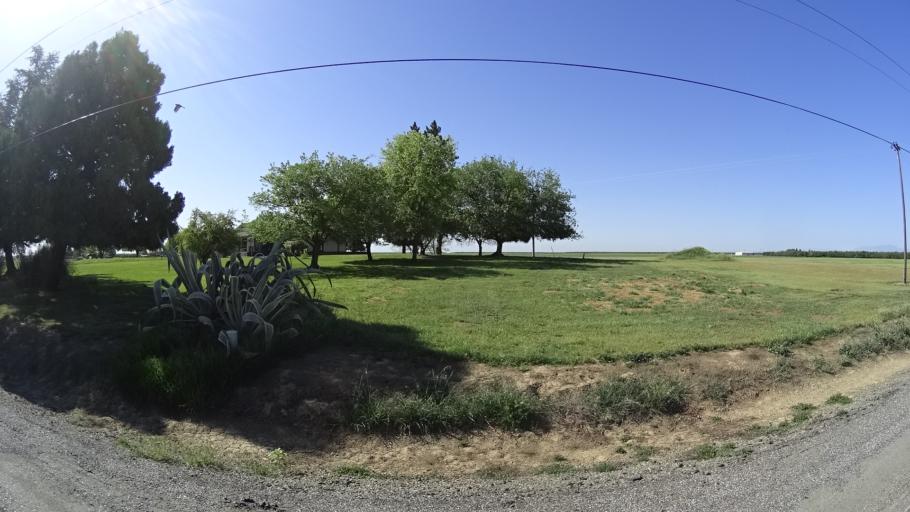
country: US
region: California
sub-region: Glenn County
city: Hamilton City
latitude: 39.7089
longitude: -122.0309
